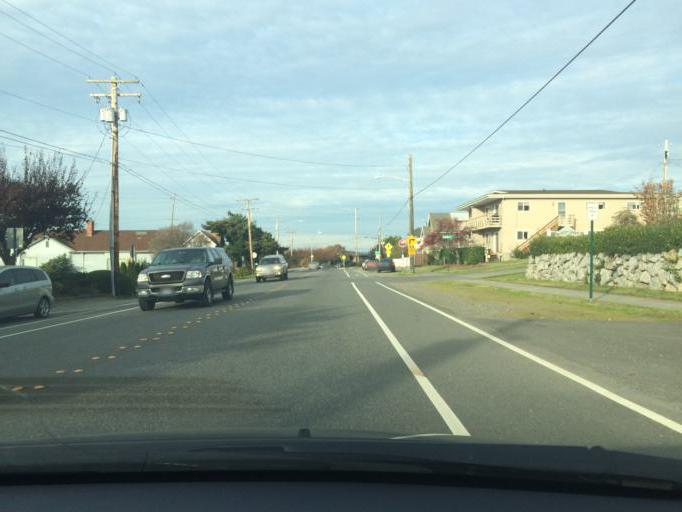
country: US
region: Washington
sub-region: Whatcom County
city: Bellingham
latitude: 48.7271
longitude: -122.5038
